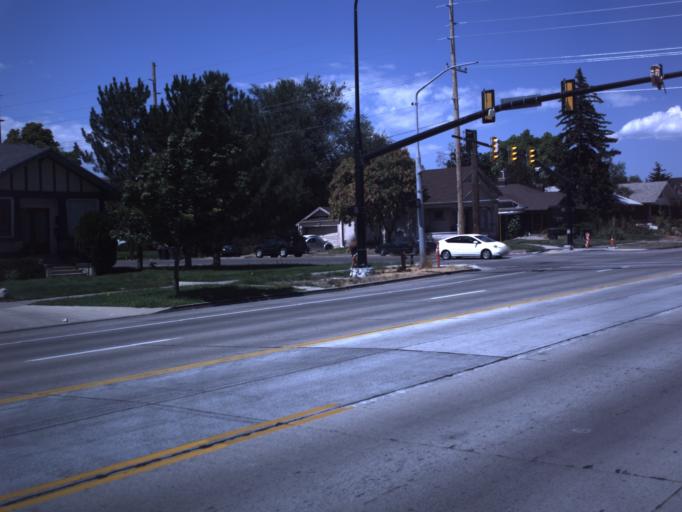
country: US
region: Utah
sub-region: Utah County
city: Provo
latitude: 40.2426
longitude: -111.6586
